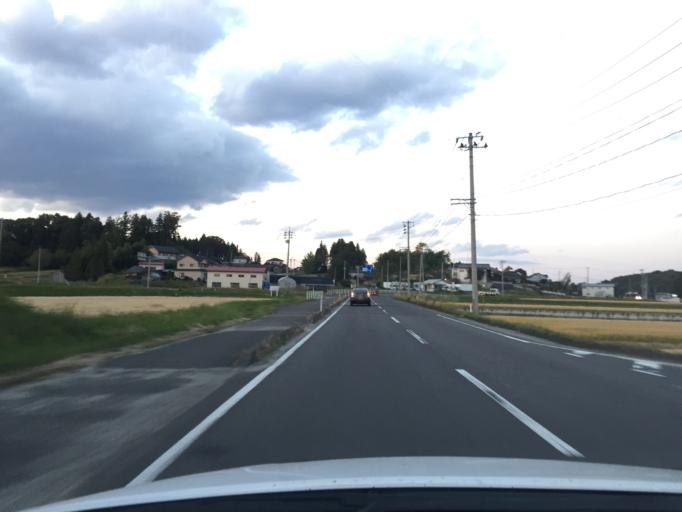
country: JP
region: Fukushima
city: Motomiya
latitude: 37.4974
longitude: 140.4543
